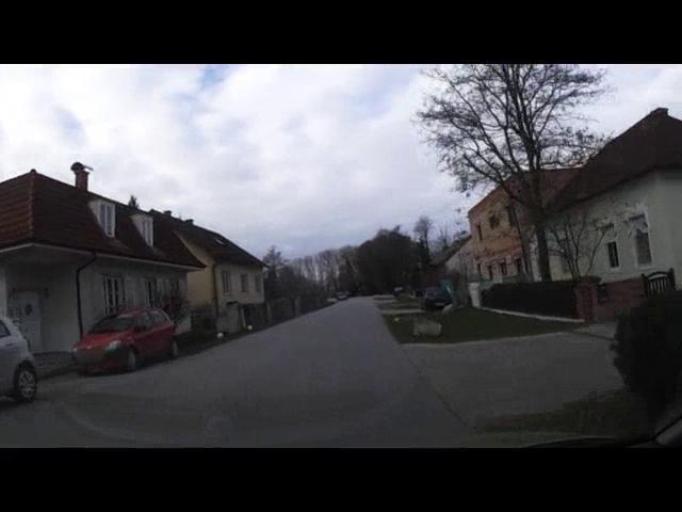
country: AT
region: Lower Austria
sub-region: Politischer Bezirk Baden
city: Pottendorf
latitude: 47.9042
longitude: 16.3580
